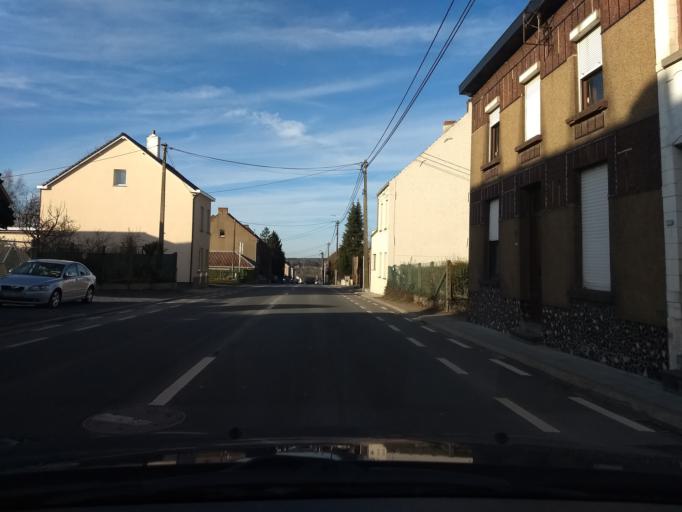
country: BE
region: Wallonia
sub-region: Province du Brabant Wallon
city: Braine-le-Chateau
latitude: 50.6714
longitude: 4.2764
